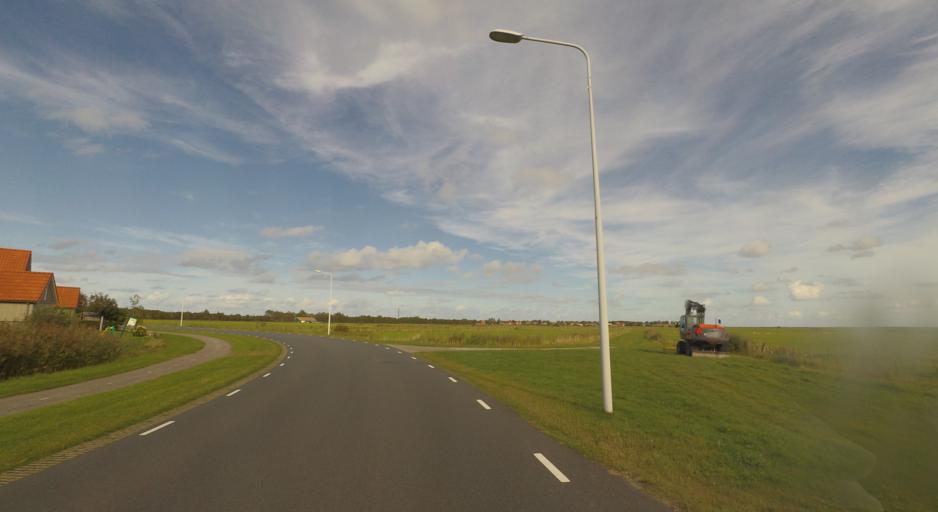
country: NL
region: Friesland
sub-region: Gemeente Ameland
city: Nes
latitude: 53.4432
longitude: 5.7818
